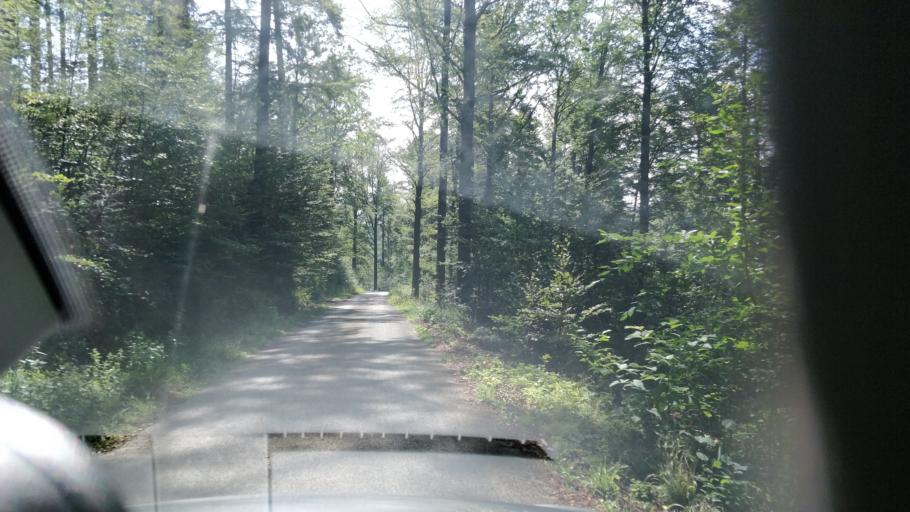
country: DE
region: Baden-Wuerttemberg
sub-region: Regierungsbezirk Stuttgart
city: Oberrot
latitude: 48.9896
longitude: 9.6721
